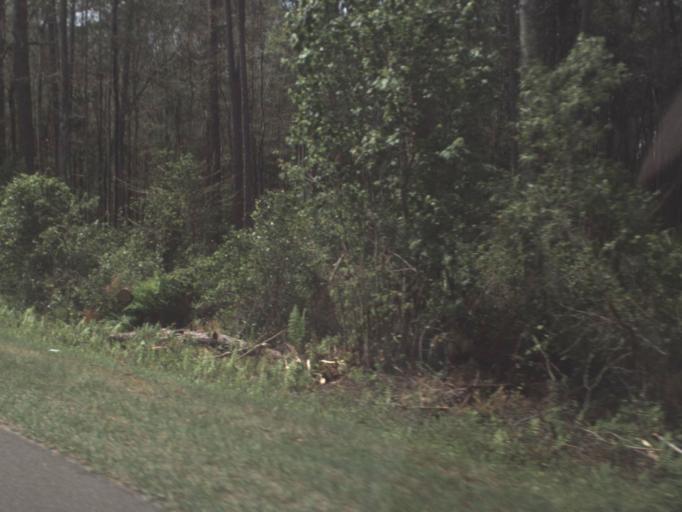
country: US
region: Florida
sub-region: Lake County
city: Umatilla
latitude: 29.0289
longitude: -81.6402
